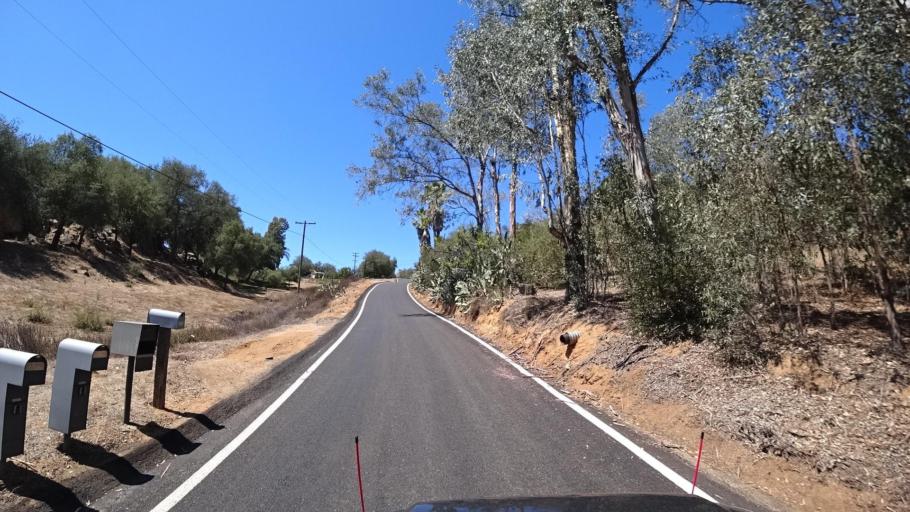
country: US
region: California
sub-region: San Diego County
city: Rainbow
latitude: 33.3846
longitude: -117.1225
